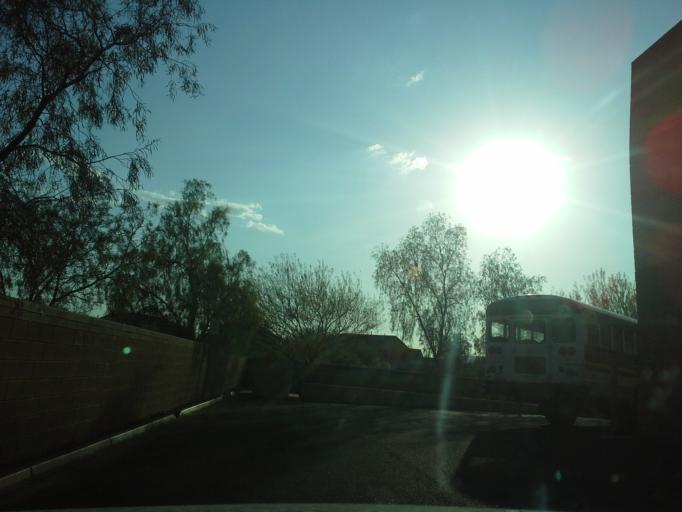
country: US
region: Arizona
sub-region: Maricopa County
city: Anthem
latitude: 33.8678
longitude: -112.1520
